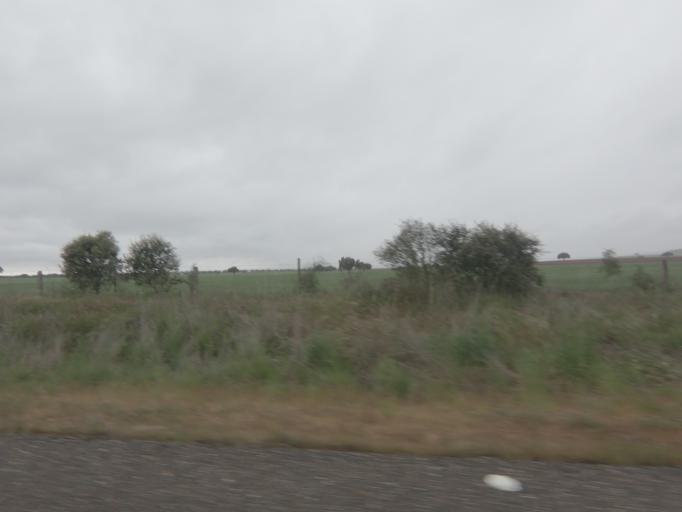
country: ES
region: Extremadura
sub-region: Provincia de Badajoz
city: La Roca de la Sierra
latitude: 39.0814
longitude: -6.7408
